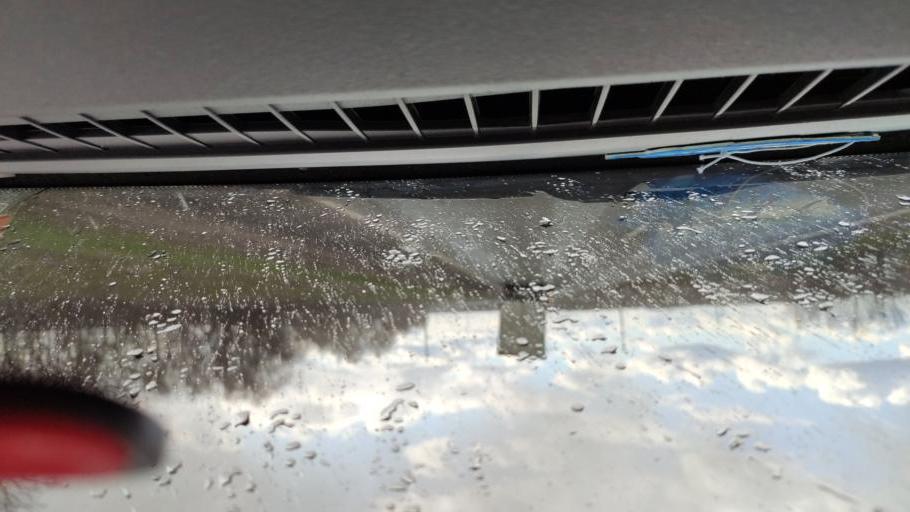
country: RU
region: Saratov
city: Balakovo
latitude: 52.1124
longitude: 47.7496
